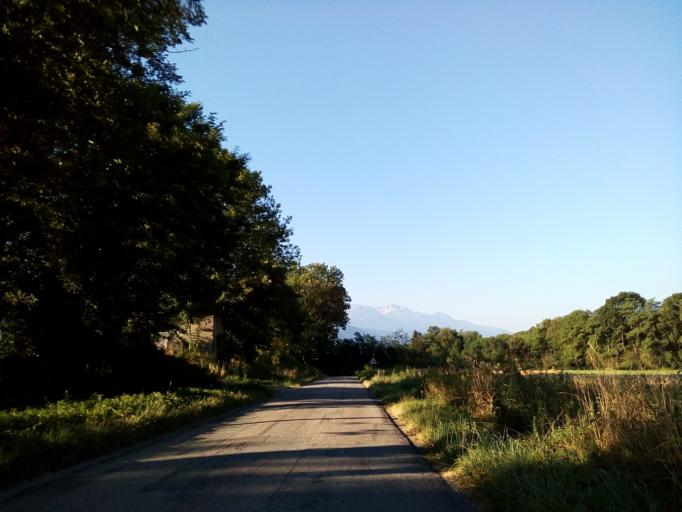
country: FR
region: Rhone-Alpes
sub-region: Departement de l'Isere
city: Barraux
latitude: 45.4251
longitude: 5.9817
